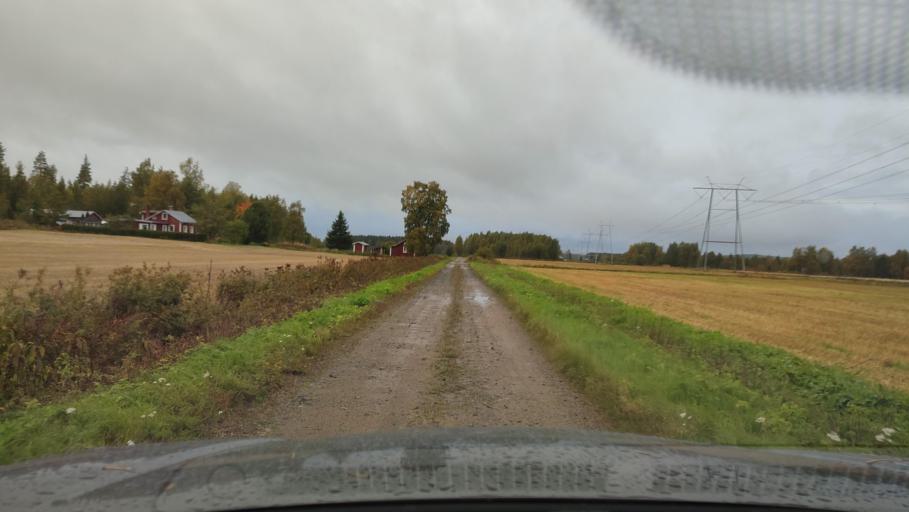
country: FI
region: Southern Ostrobothnia
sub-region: Suupohja
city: Karijoki
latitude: 62.2239
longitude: 21.6229
